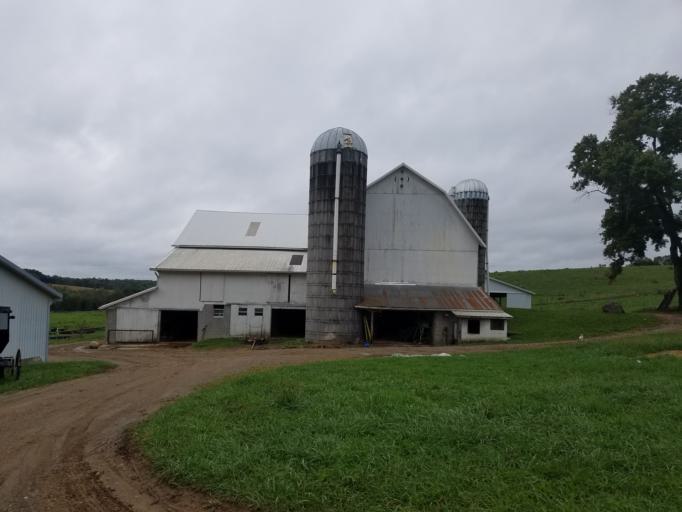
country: US
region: Ohio
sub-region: Ashland County
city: Loudonville
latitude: 40.5560
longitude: -82.2957
